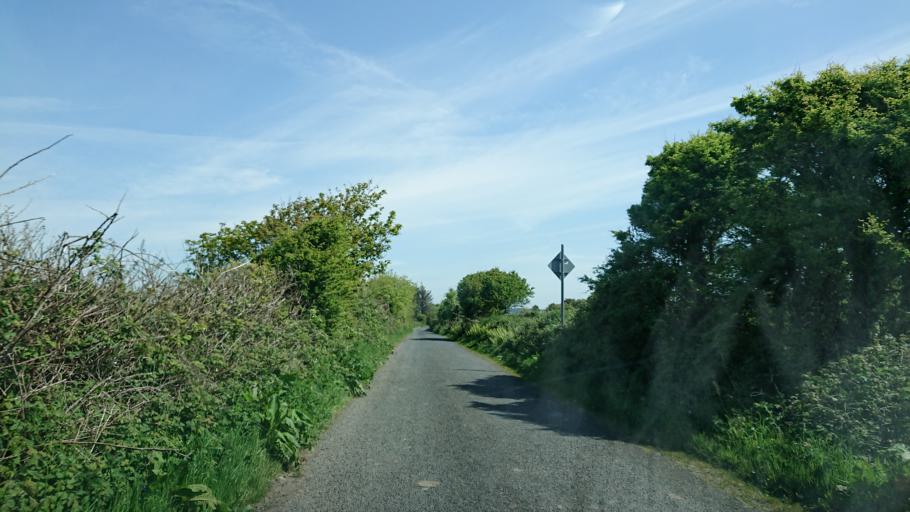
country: IE
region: Munster
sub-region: Waterford
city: Tra Mhor
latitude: 52.1515
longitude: -7.0756
